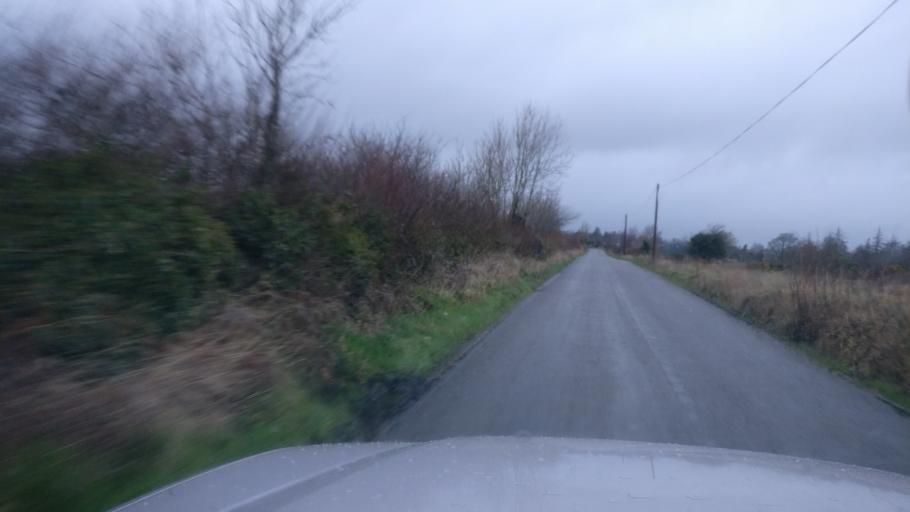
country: IE
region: Connaught
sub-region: County Galway
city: Loughrea
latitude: 53.2602
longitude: -8.4031
